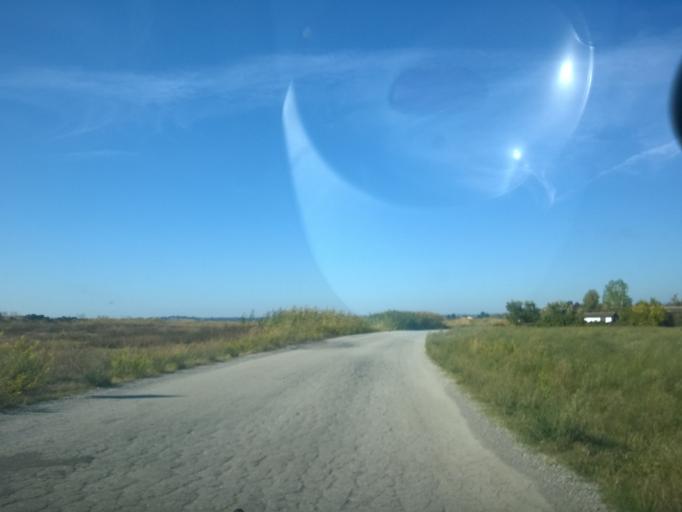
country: GR
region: Central Macedonia
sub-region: Nomos Chalkidikis
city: Nea Kallikrateia
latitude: 40.3260
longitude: 23.0229
